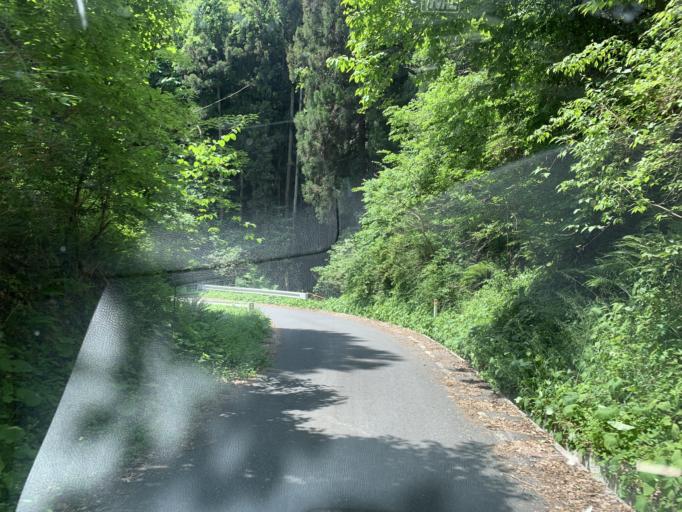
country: JP
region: Iwate
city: Ichinoseki
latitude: 38.9681
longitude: 141.2296
